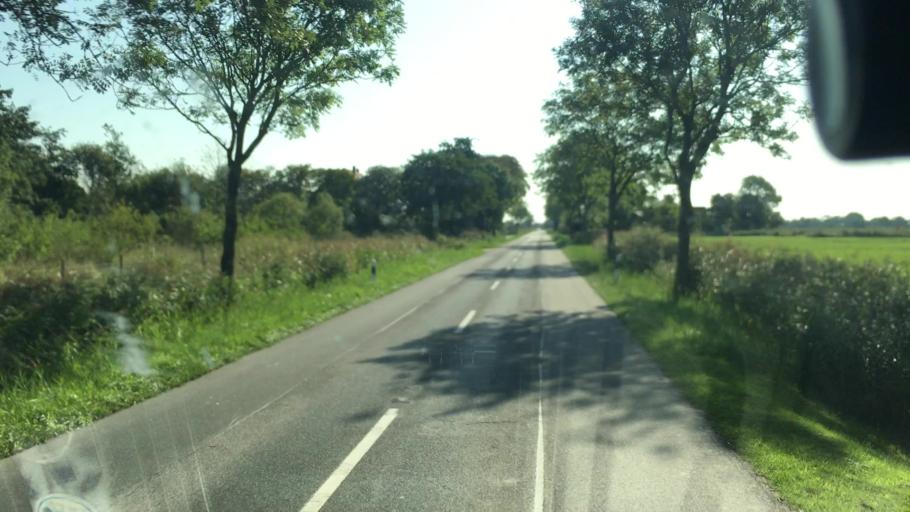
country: DE
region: Lower Saxony
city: Werdum
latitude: 53.6635
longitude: 7.6975
